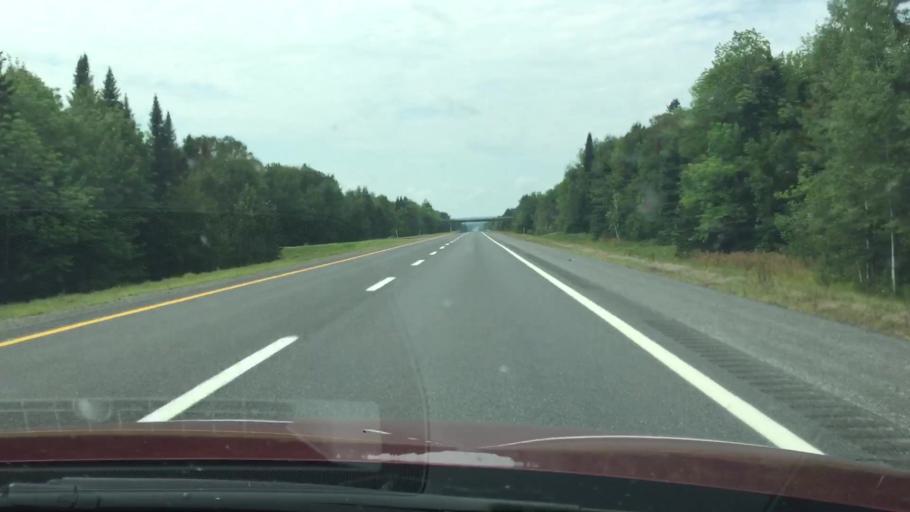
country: US
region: Maine
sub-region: Aroostook County
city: Houlton
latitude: 46.1416
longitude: -67.9510
